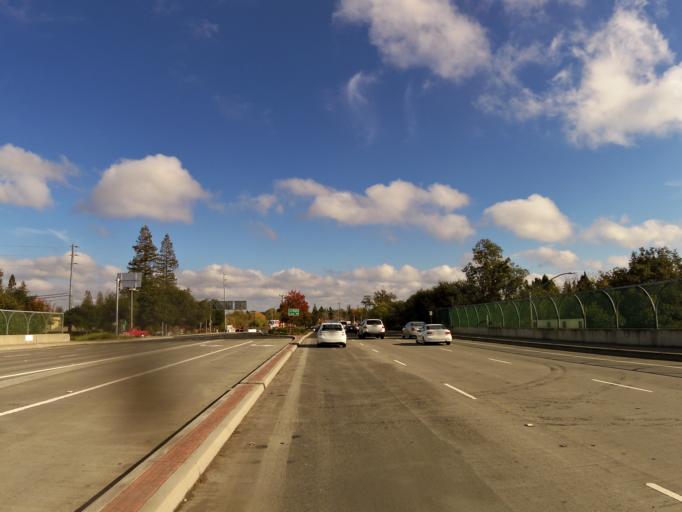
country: US
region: California
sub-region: Sacramento County
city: Elk Grove
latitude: 38.4091
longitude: -121.3889
